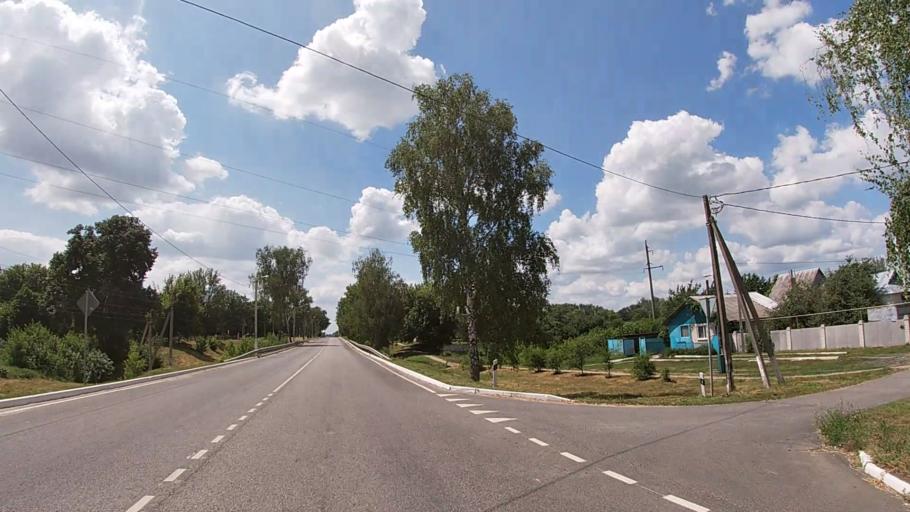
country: RU
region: Belgorod
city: Grayvoron
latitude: 50.4880
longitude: 35.6923
